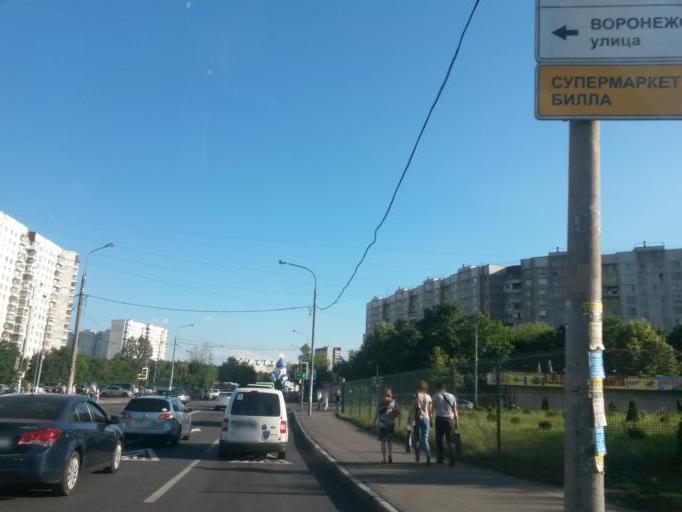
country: RU
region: Moscow
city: Orekhovo-Borisovo
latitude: 55.6111
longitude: 37.7446
